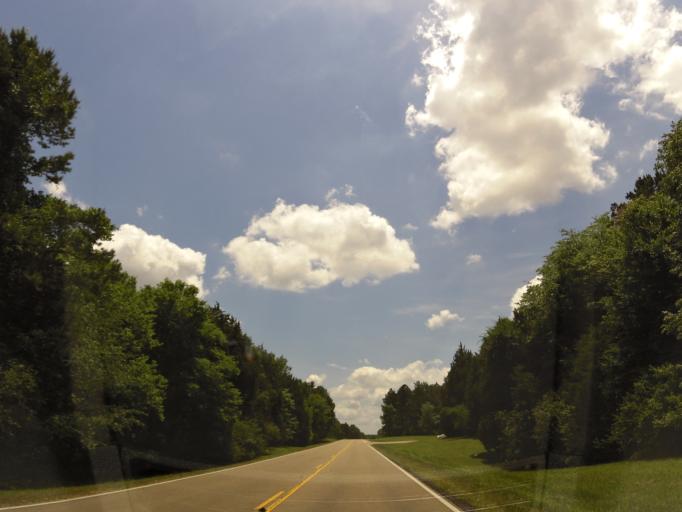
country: US
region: Mississippi
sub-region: Lee County
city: Tupelo
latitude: 34.2555
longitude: -88.7565
